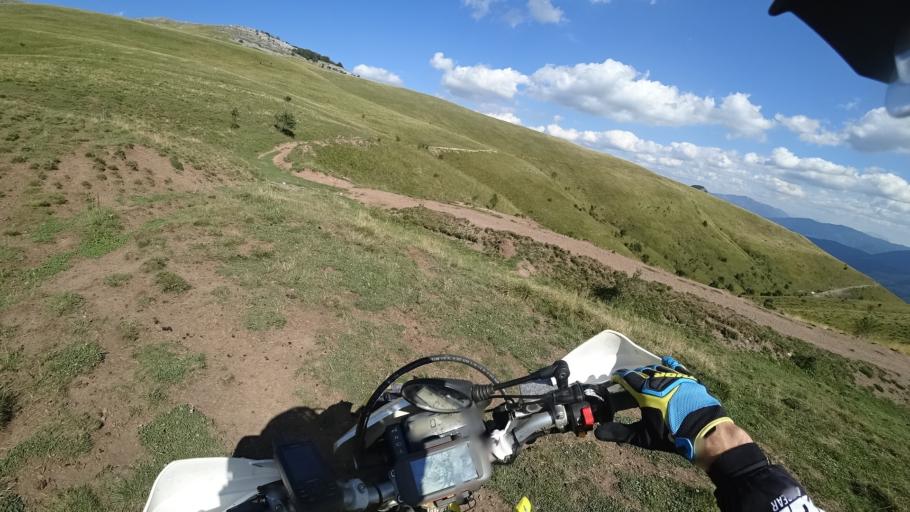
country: HR
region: Zadarska
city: Gracac
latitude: 44.3968
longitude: 16.0127
